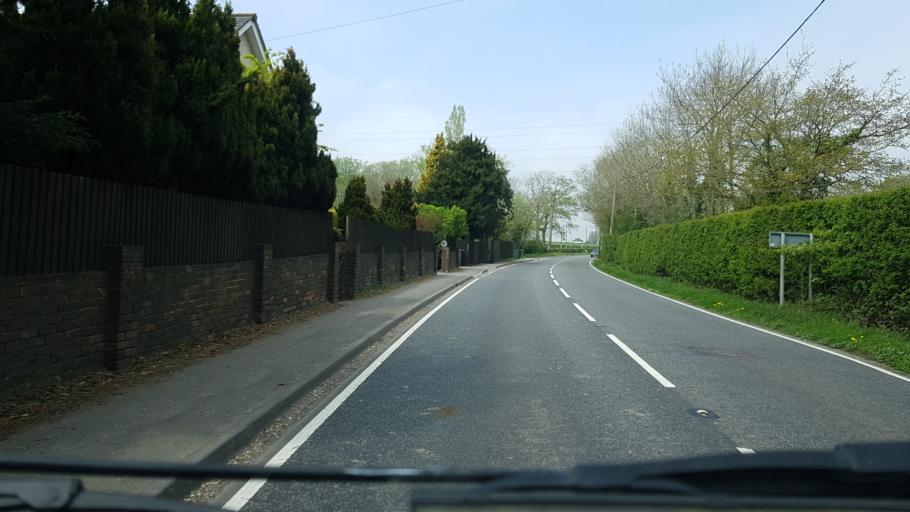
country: GB
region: England
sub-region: Hampshire
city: Kingsclere
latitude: 51.3311
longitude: -1.2535
